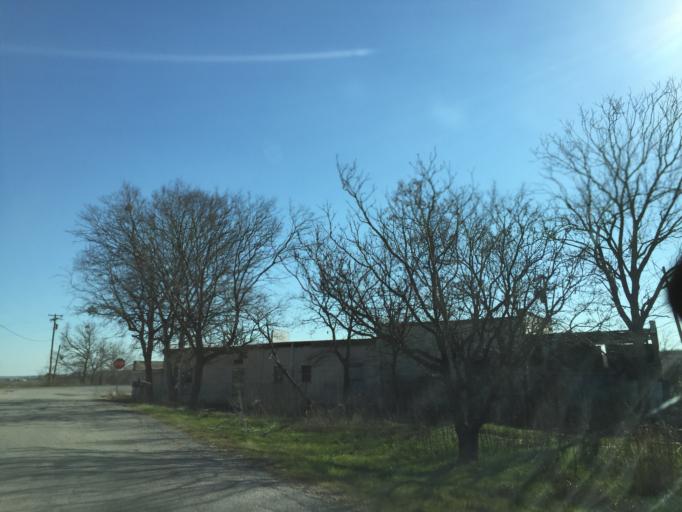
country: US
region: Texas
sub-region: Williamson County
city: Taylor
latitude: 30.5585
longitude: -97.3048
